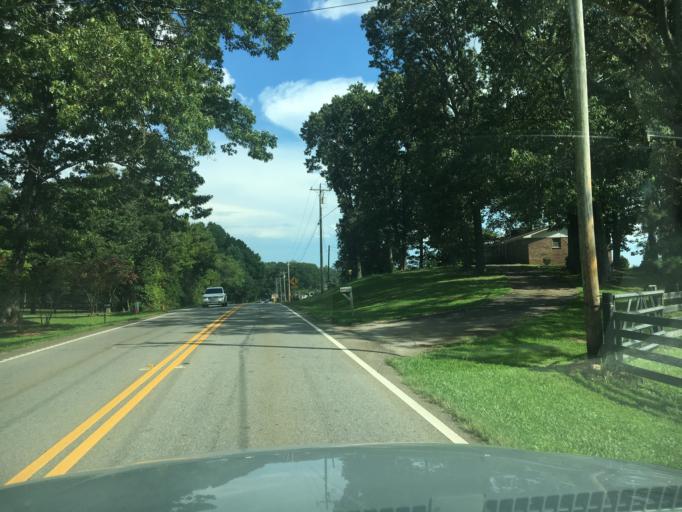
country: US
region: Georgia
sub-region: Cherokee County
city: Holly Springs
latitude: 34.1901
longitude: -84.4413
